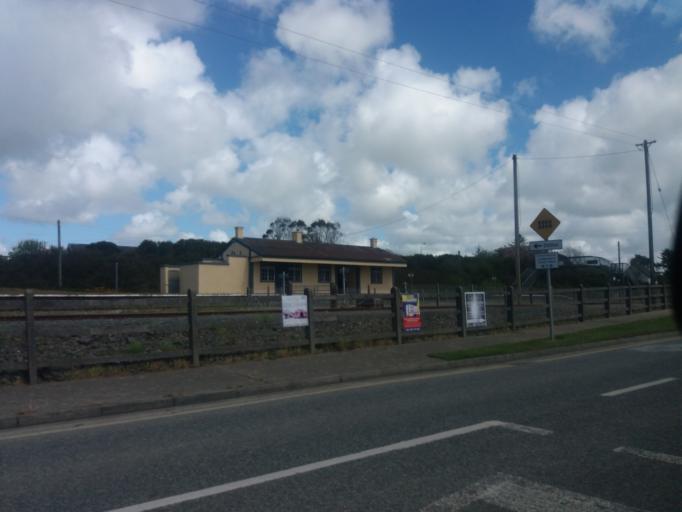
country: IE
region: Leinster
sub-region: Loch Garman
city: New Ross
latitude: 52.2673
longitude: -6.7547
